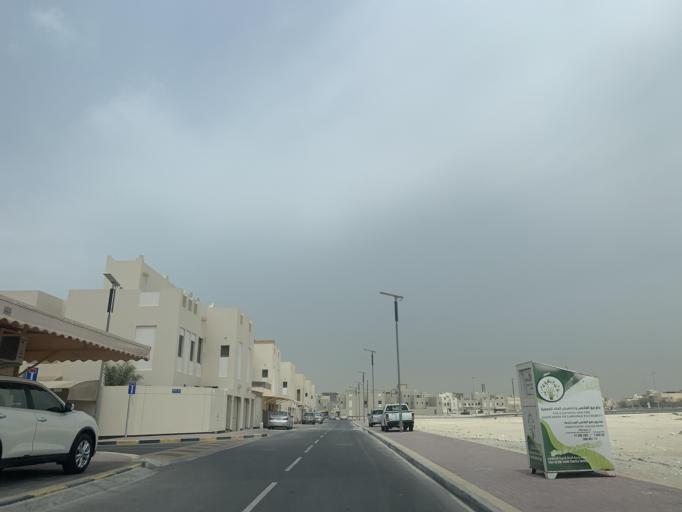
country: BH
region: Northern
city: Madinat `Isa
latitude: 26.1753
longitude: 50.5185
